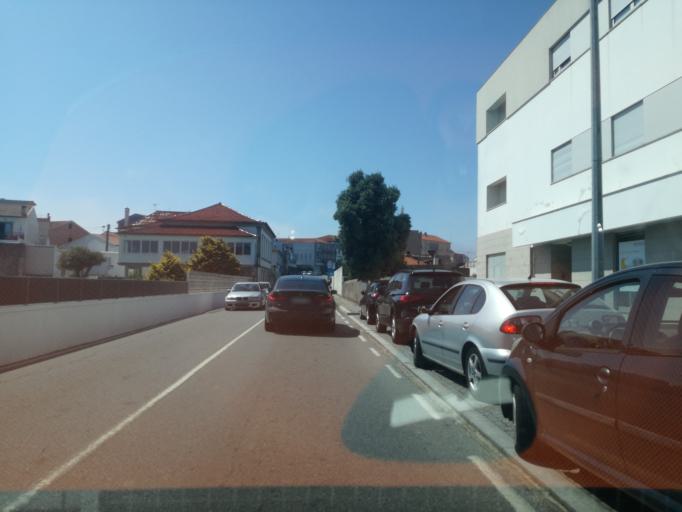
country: PT
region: Braga
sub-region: Esposende
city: Apulia
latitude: 41.5106
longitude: -8.7700
